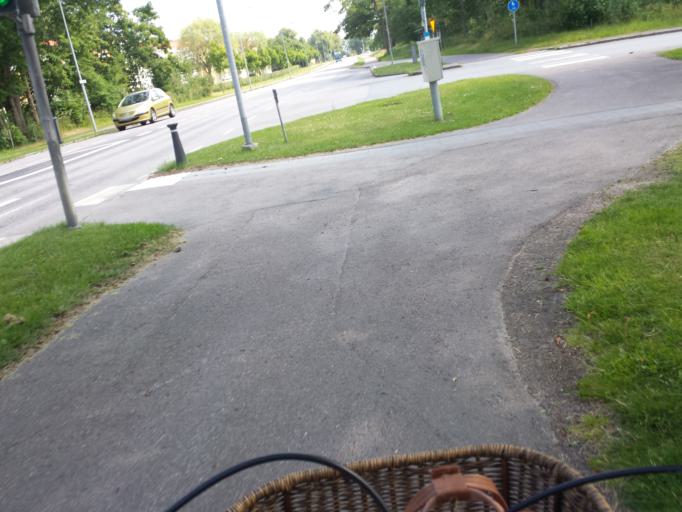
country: SE
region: Kalmar
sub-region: Kalmar Kommun
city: Kalmar
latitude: 56.6800
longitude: 16.3449
